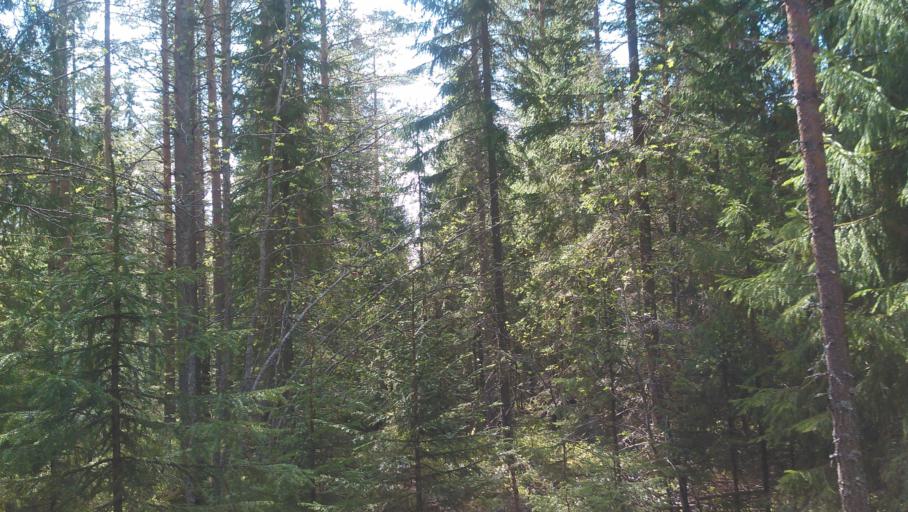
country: SE
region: Vaesterbotten
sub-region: Umea Kommun
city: Umea
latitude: 63.8368
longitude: 20.2990
